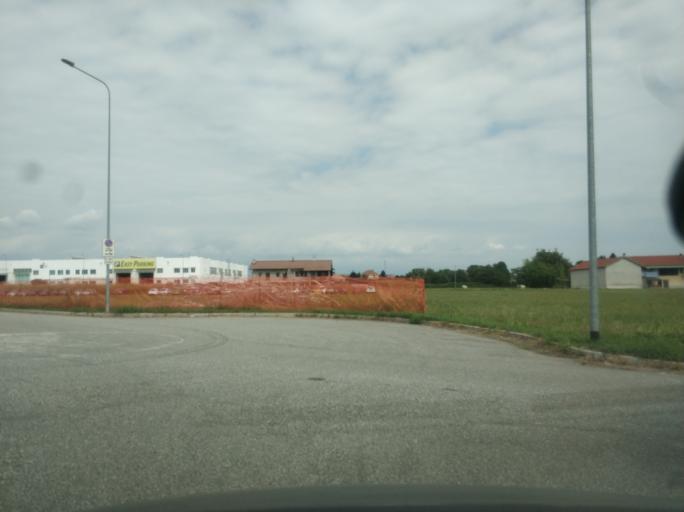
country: IT
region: Piedmont
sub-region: Provincia di Torino
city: Caselle Torinese
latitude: 45.1775
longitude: 7.6612
